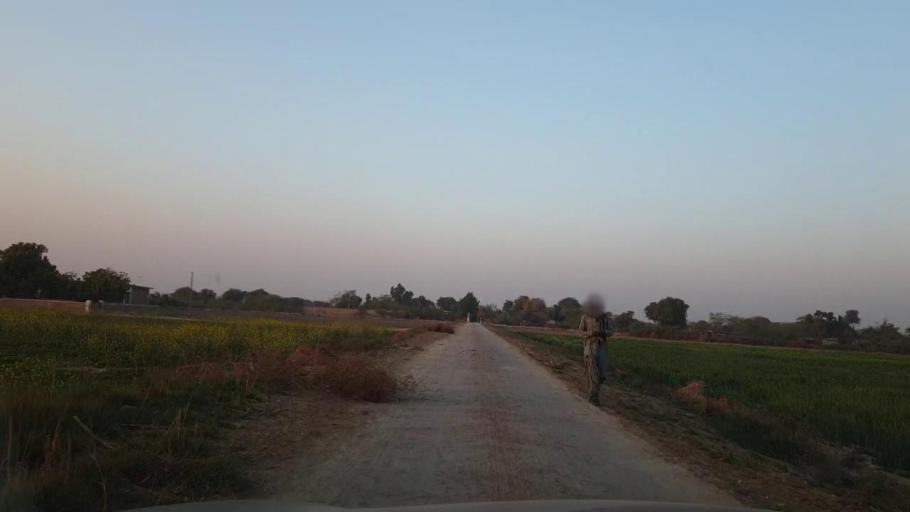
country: PK
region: Sindh
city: Mirpur Khas
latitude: 25.5965
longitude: 68.8523
